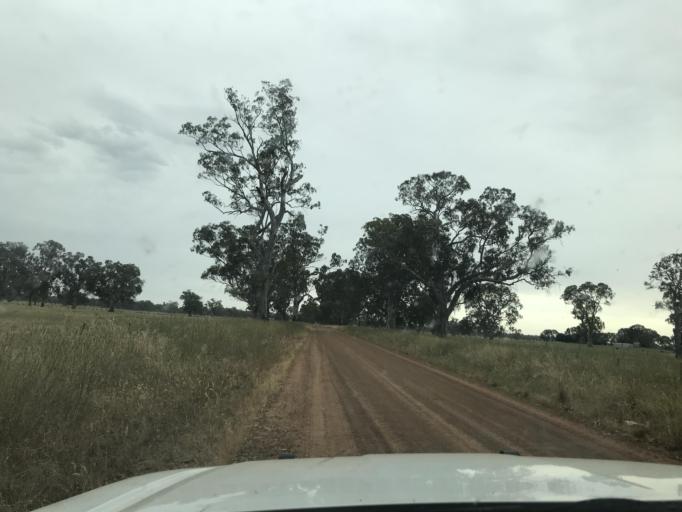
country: AU
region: South Australia
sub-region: Wattle Range
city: Penola
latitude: -37.1347
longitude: 141.5589
